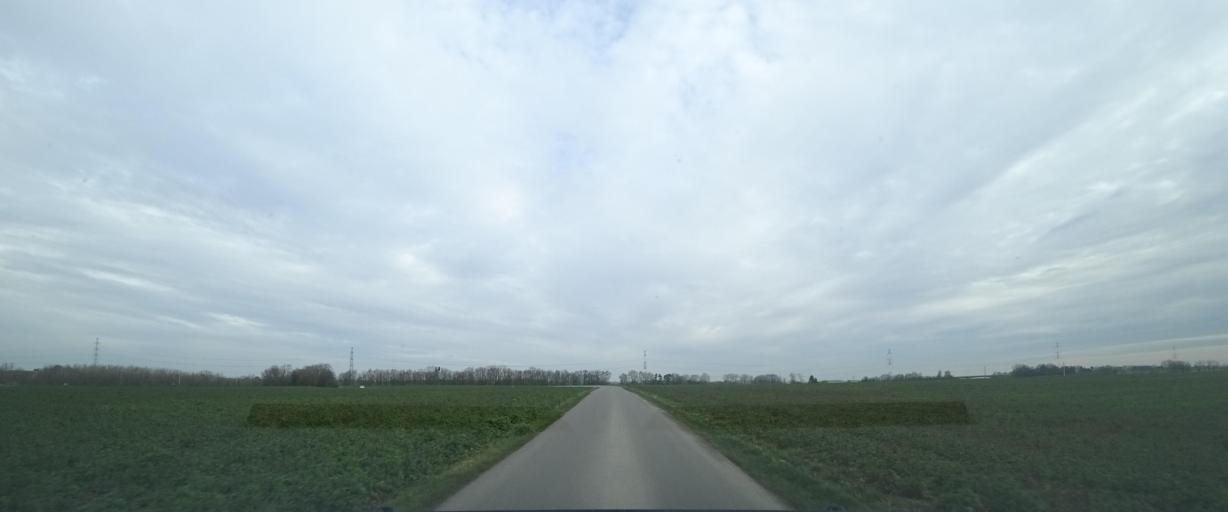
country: BE
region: Wallonia
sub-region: Province de Namur
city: Sombreffe
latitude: 50.4886
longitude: 4.6337
